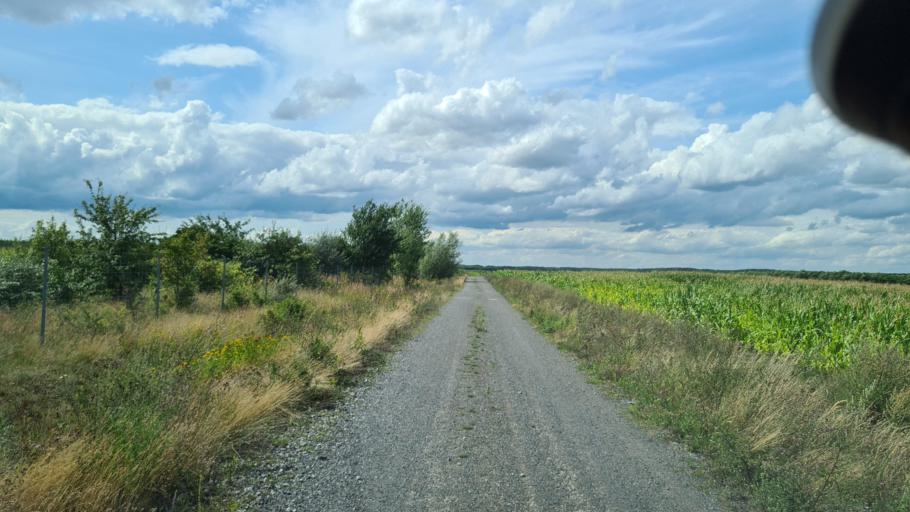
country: DE
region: Brandenburg
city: Spremberg
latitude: 51.6029
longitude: 14.2953
